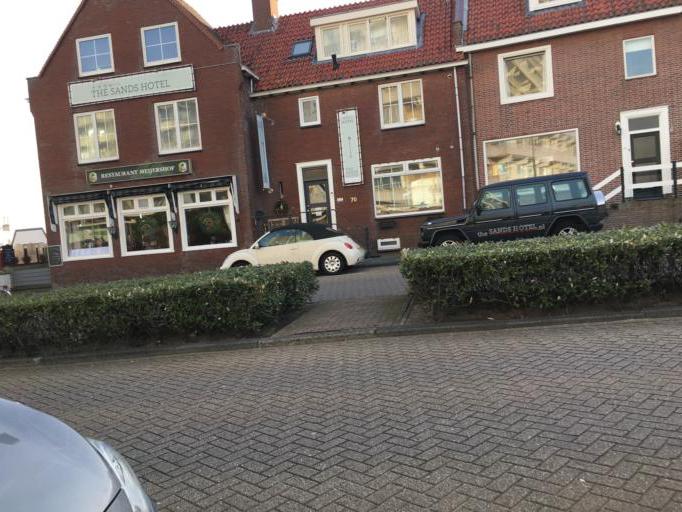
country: NL
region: North Holland
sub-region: Gemeente Zandvoort
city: Zandvoort
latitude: 52.3745
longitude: 4.5286
